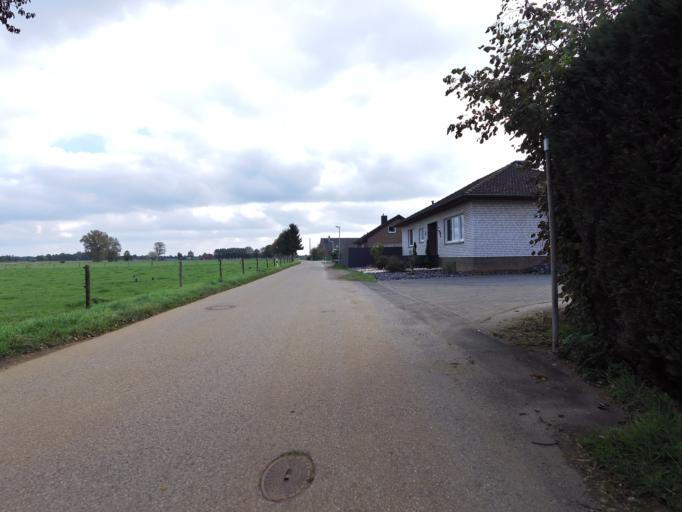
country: DE
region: North Rhine-Westphalia
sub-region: Regierungsbezirk Munster
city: Isselburg
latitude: 51.8290
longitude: 6.4719
